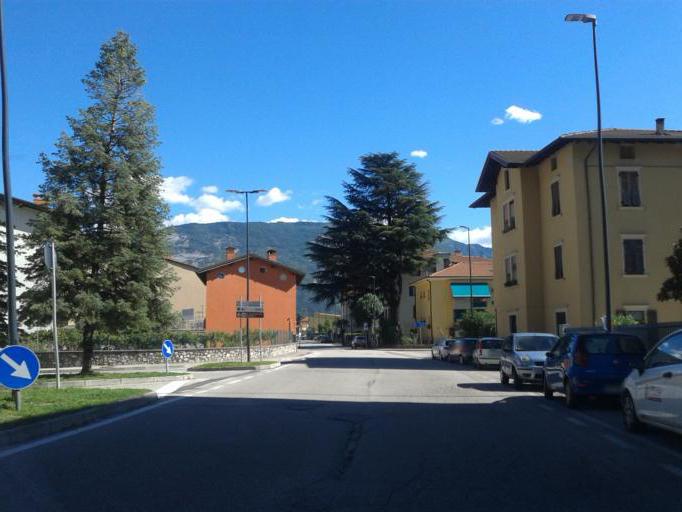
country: IT
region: Trentino-Alto Adige
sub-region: Provincia di Trento
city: Mori
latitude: 45.8542
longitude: 10.9726
